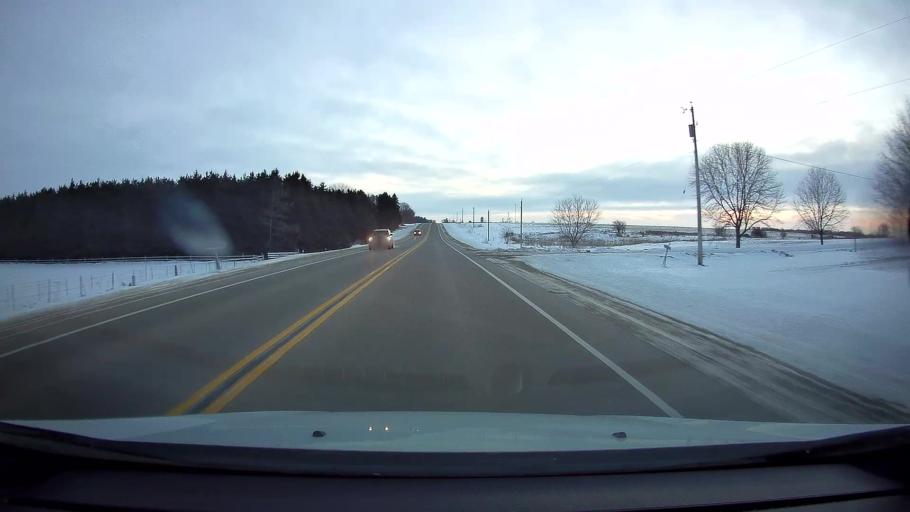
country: US
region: Wisconsin
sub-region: Saint Croix County
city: New Richmond
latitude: 45.1372
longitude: -92.4961
